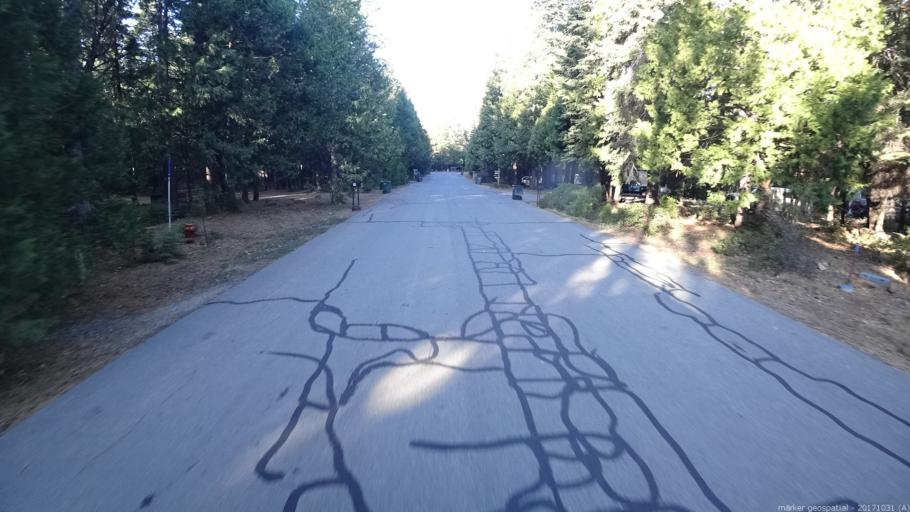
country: US
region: California
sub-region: Shasta County
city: Shingletown
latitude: 40.5248
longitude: -121.7987
